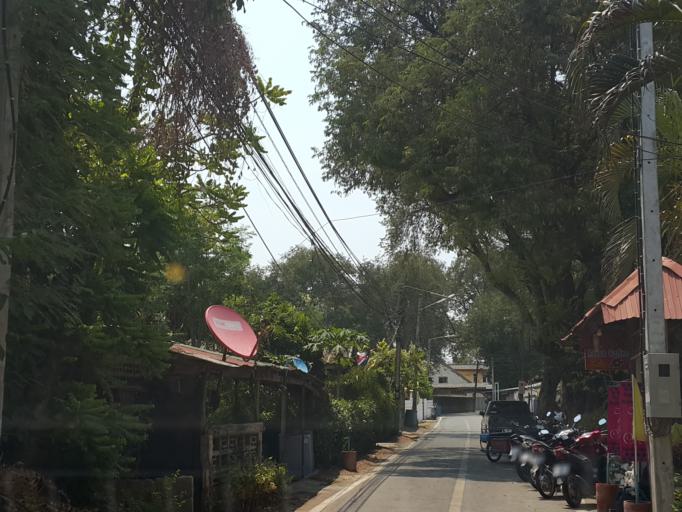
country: TH
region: Kanchanaburi
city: Kanchanaburi
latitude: 14.0301
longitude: 99.5226
